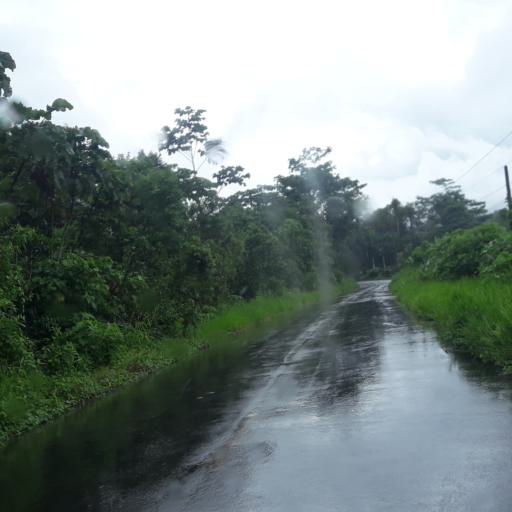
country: EC
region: Napo
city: Tena
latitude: -1.0400
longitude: -77.6639
